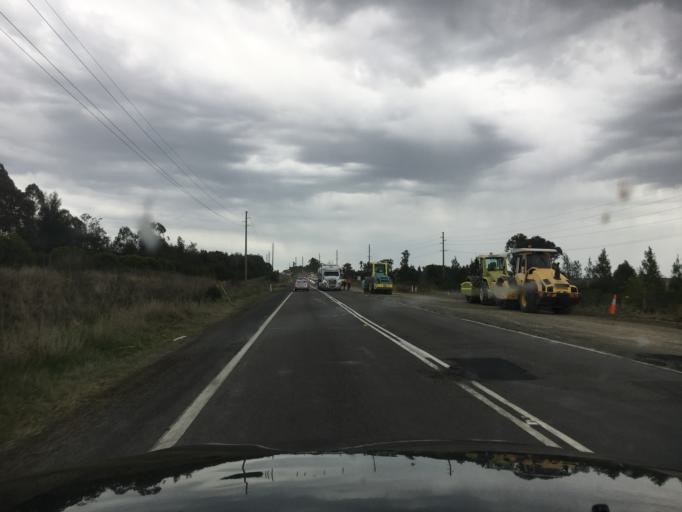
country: AU
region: New South Wales
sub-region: Muswellbrook
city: Muswellbrook
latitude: -32.1982
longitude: 150.8930
